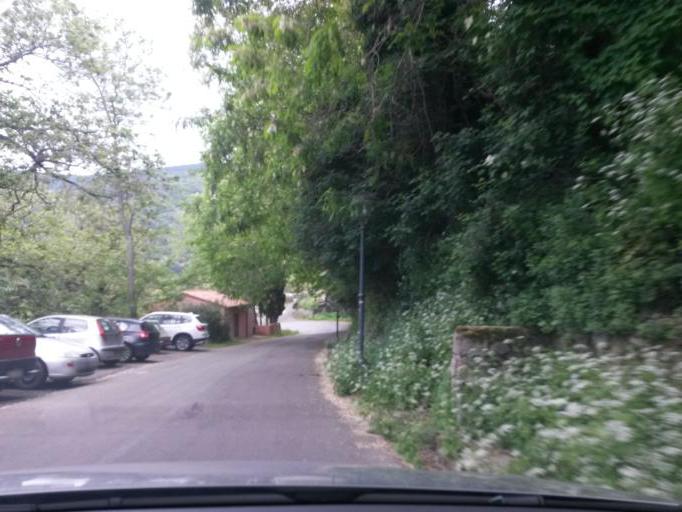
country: IT
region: Tuscany
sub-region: Provincia di Livorno
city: Marciana
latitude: 42.7864
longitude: 10.1846
